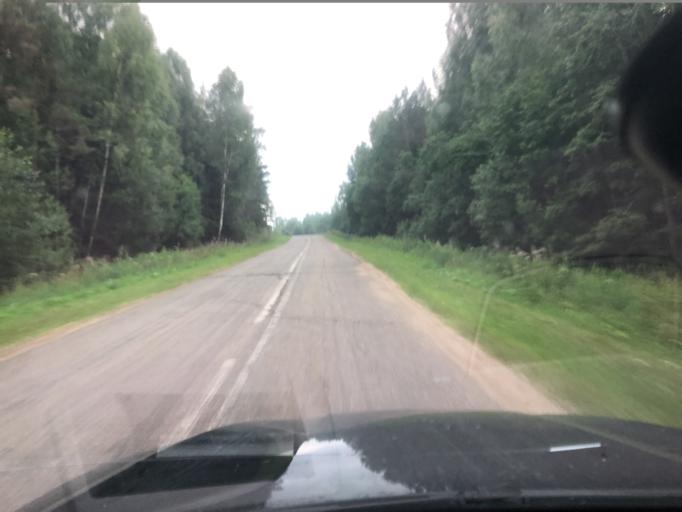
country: RU
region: Jaroslavl
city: Pereslavl'-Zalesskiy
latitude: 57.0348
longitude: 38.9075
